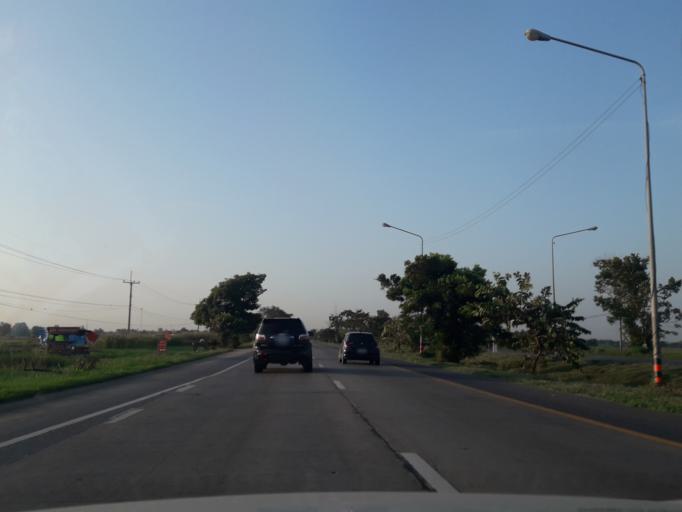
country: TH
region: Phra Nakhon Si Ayutthaya
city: Phra Nakhon Si Ayutthaya
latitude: 14.2999
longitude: 100.5252
